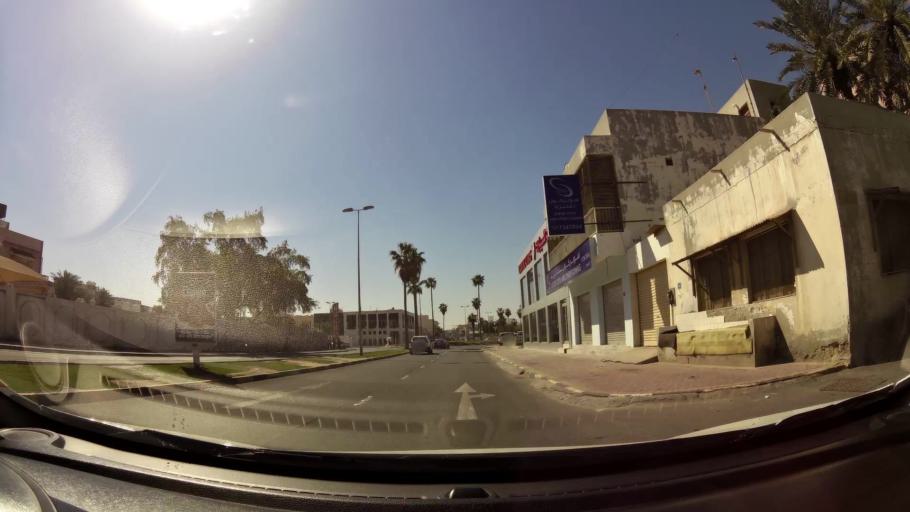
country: BH
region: Muharraq
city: Al Muharraq
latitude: 26.2543
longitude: 50.6081
